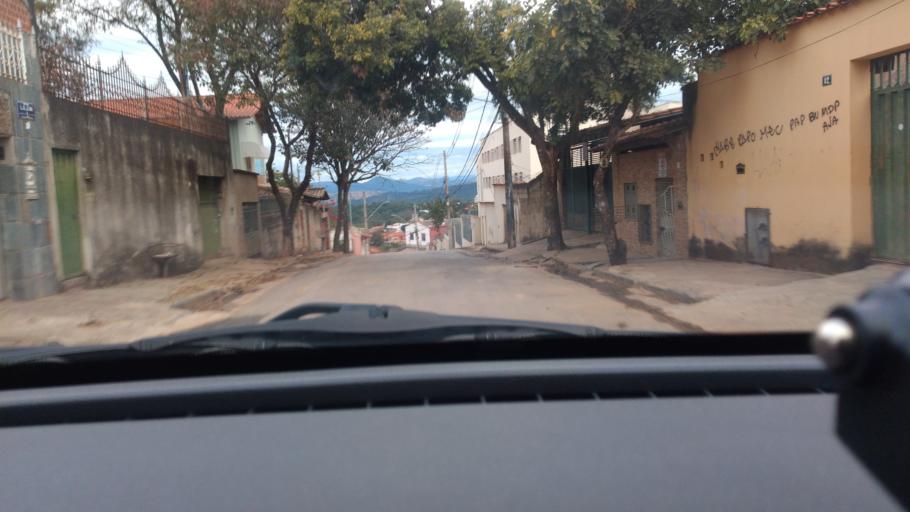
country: BR
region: Minas Gerais
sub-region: Santa Luzia
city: Santa Luzia
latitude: -19.8089
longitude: -43.9391
